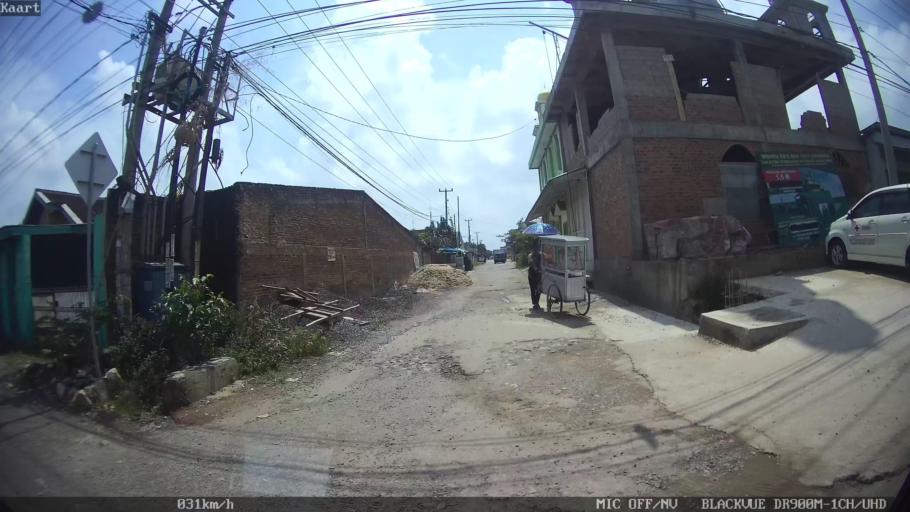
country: ID
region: Lampung
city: Kedaton
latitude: -5.3562
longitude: 105.3010
